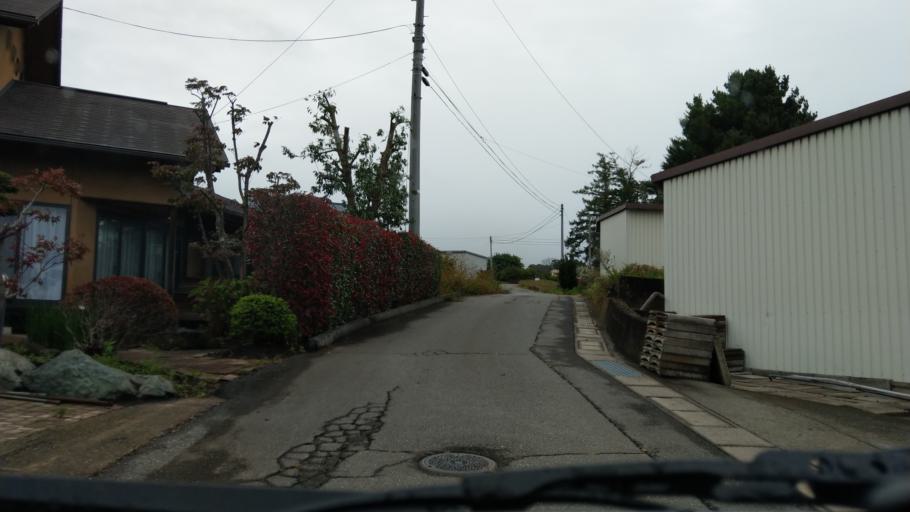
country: JP
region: Nagano
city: Komoro
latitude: 36.3348
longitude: 138.4516
